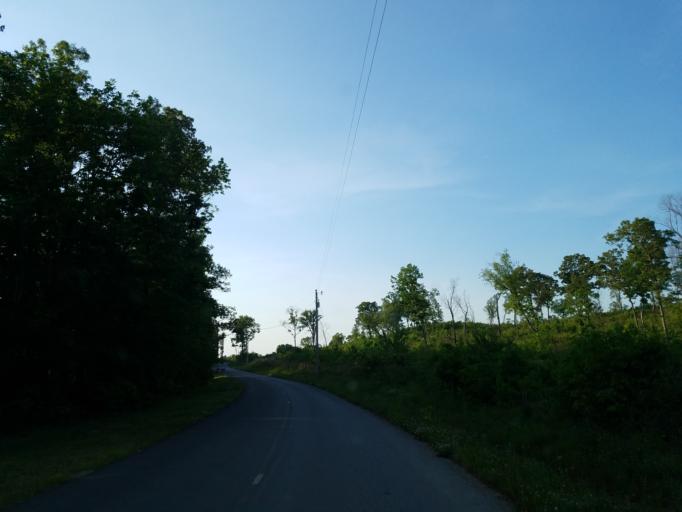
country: US
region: Georgia
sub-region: Whitfield County
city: Dalton
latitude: 34.6664
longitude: -85.0789
